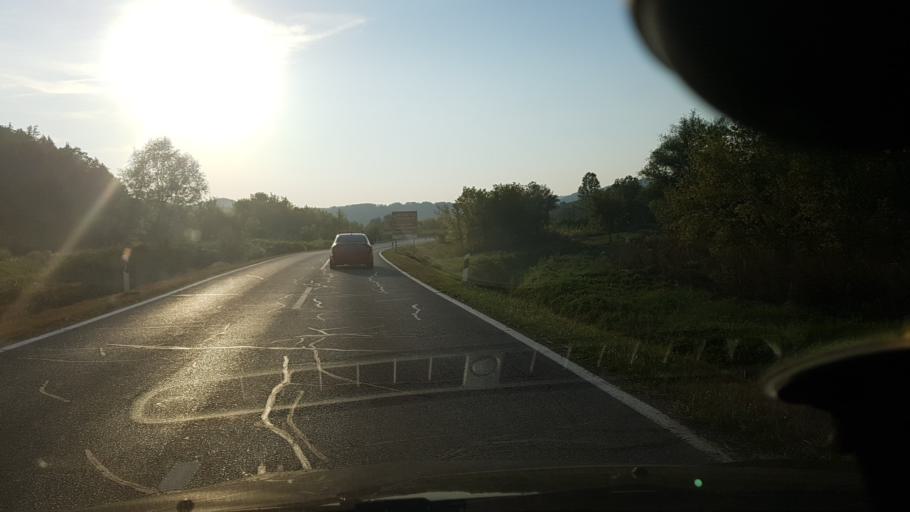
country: HR
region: Krapinsko-Zagorska
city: Pregrada
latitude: 46.1414
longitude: 15.7861
